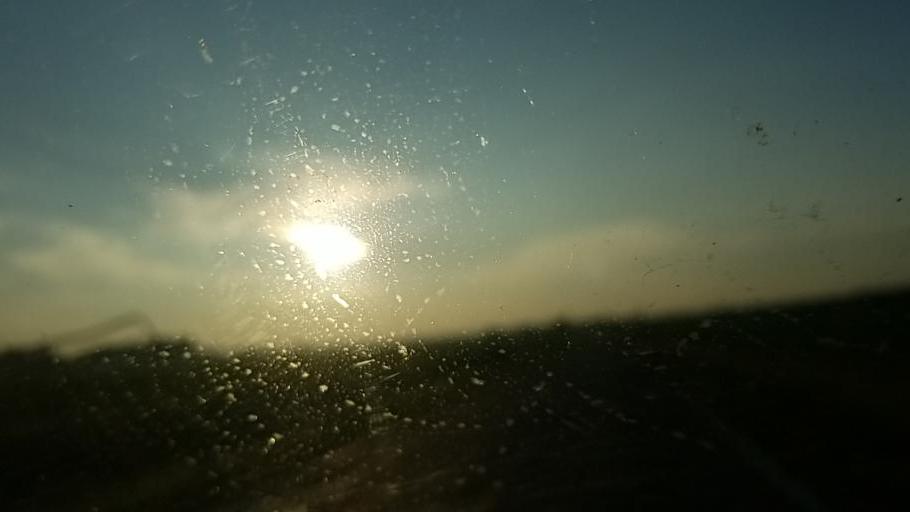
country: US
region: Michigan
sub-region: Montcalm County
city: Howard City
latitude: 43.3591
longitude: -85.3831
